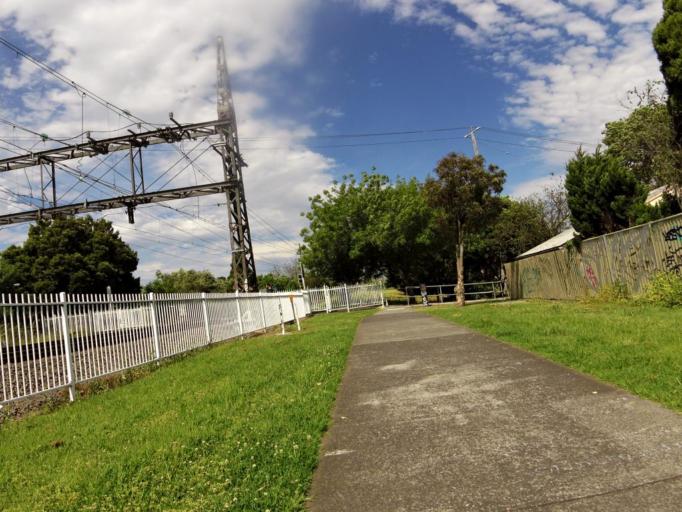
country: AU
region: Victoria
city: Hughesdale
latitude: -37.8978
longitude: 145.0839
